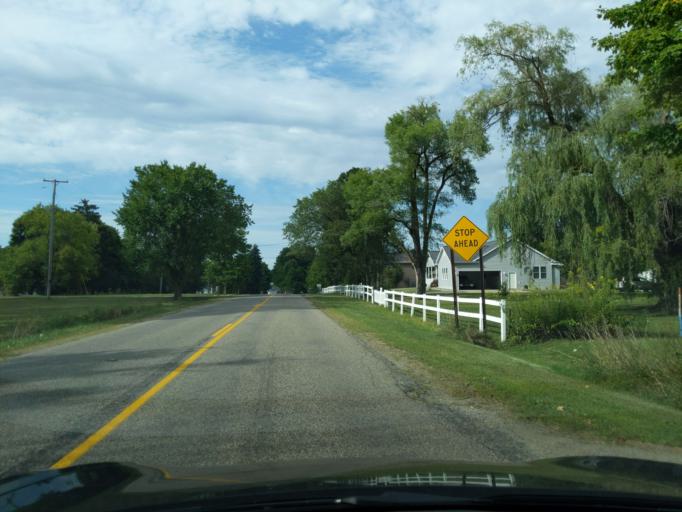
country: US
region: Michigan
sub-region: Eaton County
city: Dimondale
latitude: 42.6809
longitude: -84.6228
